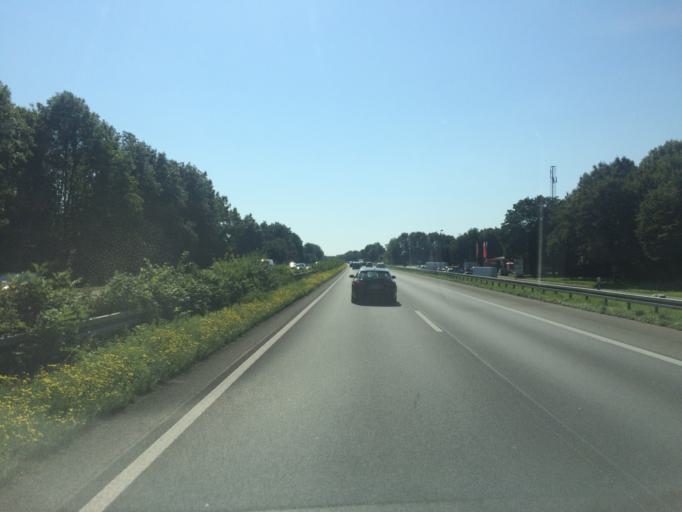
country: DE
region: North Rhine-Westphalia
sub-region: Regierungsbezirk Munster
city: Ascheberg
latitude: 51.7754
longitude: 7.6395
